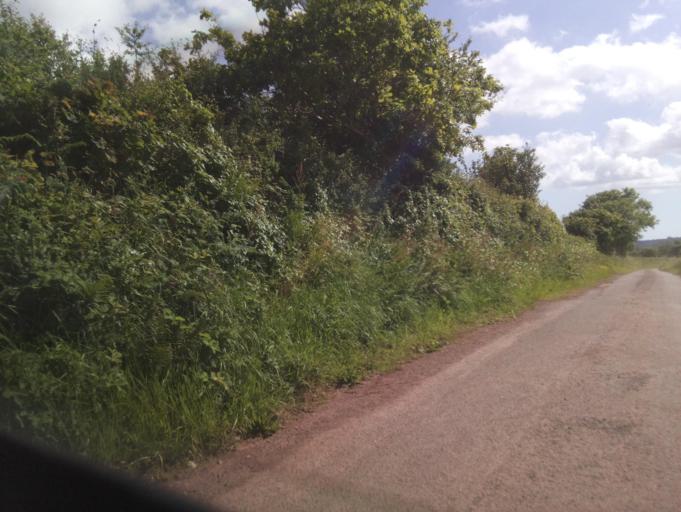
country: GB
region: England
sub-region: Devon
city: Totnes
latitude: 50.4036
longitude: -3.7036
